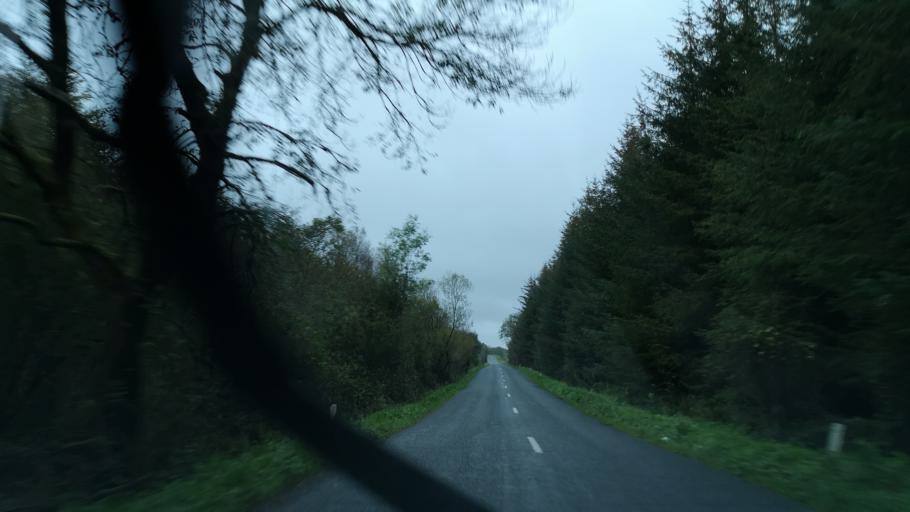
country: IE
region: Connaught
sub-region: Maigh Eo
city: Ballyhaunis
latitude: 53.7950
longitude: -8.7054
